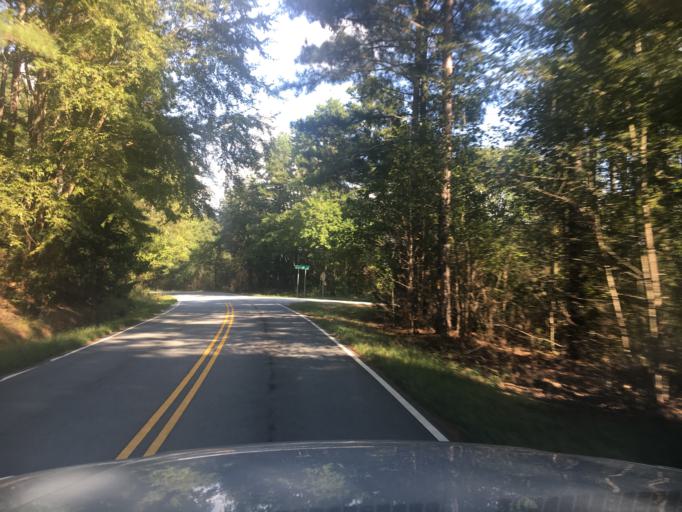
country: US
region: South Carolina
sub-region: Pickens County
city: Liberty
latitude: 34.7150
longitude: -82.6880
